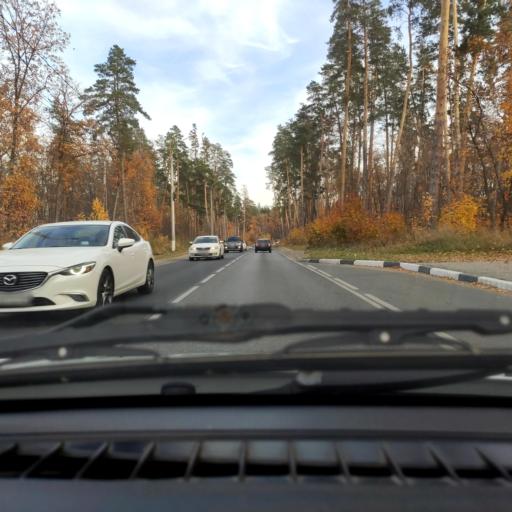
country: RU
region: Samara
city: Tol'yatti
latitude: 53.4923
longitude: 49.3012
